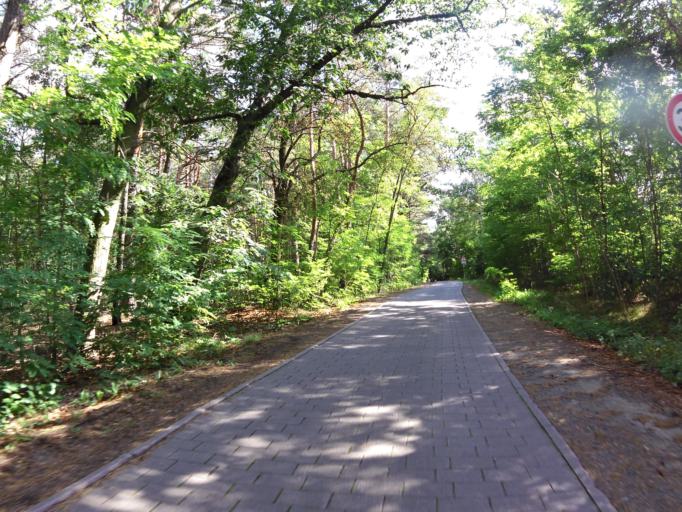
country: DE
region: Brandenburg
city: Munchehofe
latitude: 52.1910
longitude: 13.8795
